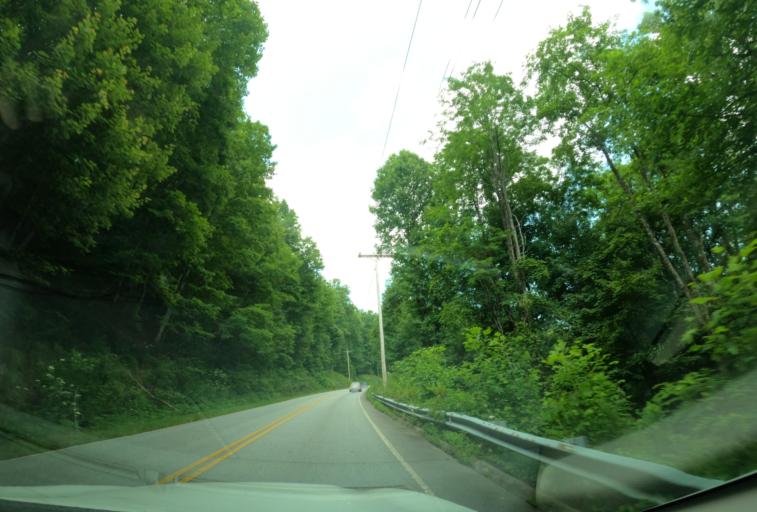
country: US
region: North Carolina
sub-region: Jackson County
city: Cullowhee
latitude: 35.0831
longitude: -82.9910
